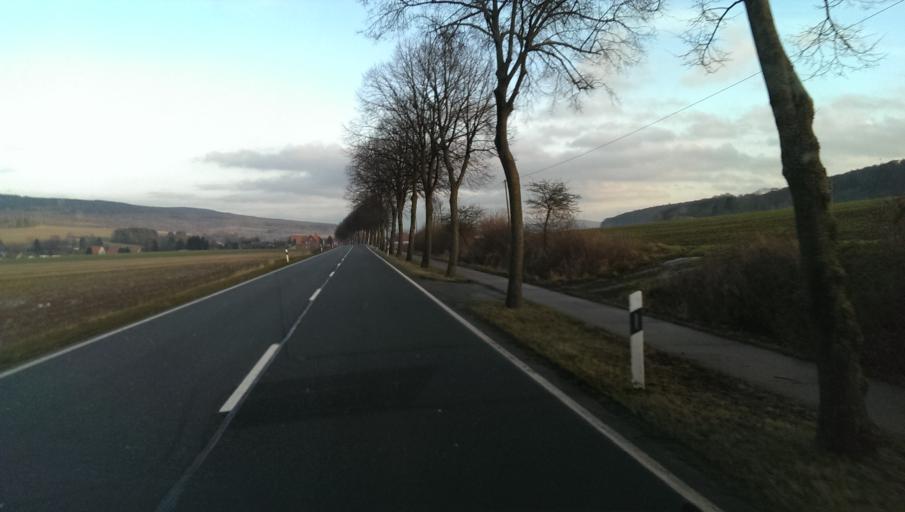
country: DE
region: Lower Saxony
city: Eimen
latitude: 51.8875
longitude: 9.7397
